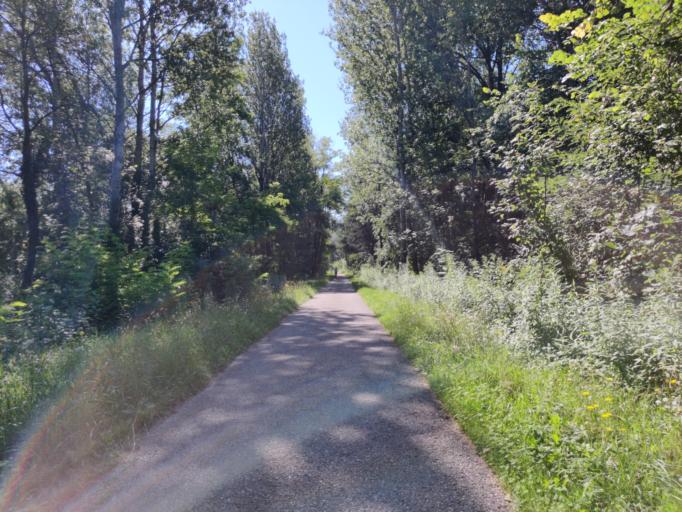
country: AT
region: Styria
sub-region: Politischer Bezirk Graz-Umgebung
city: Werndorf
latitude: 46.9002
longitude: 15.4944
